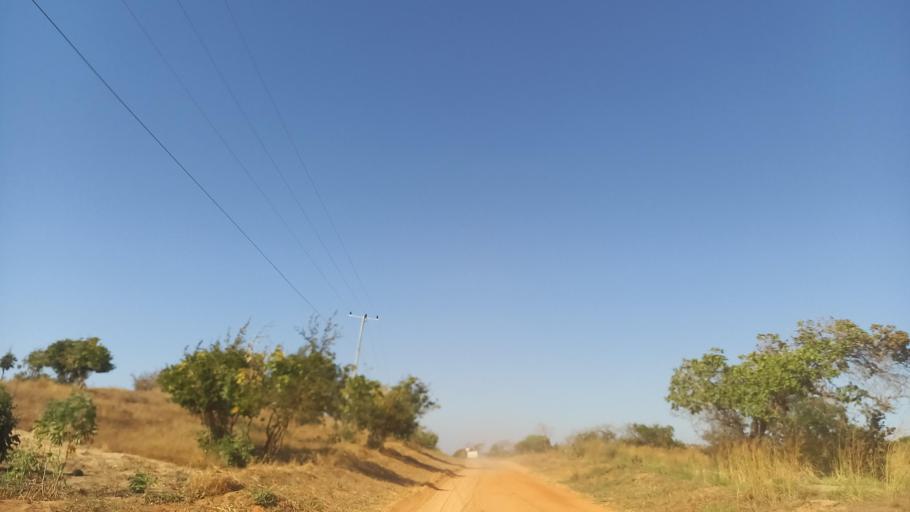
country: MZ
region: Cabo Delgado
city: Pemba
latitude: -13.1611
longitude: 40.5589
